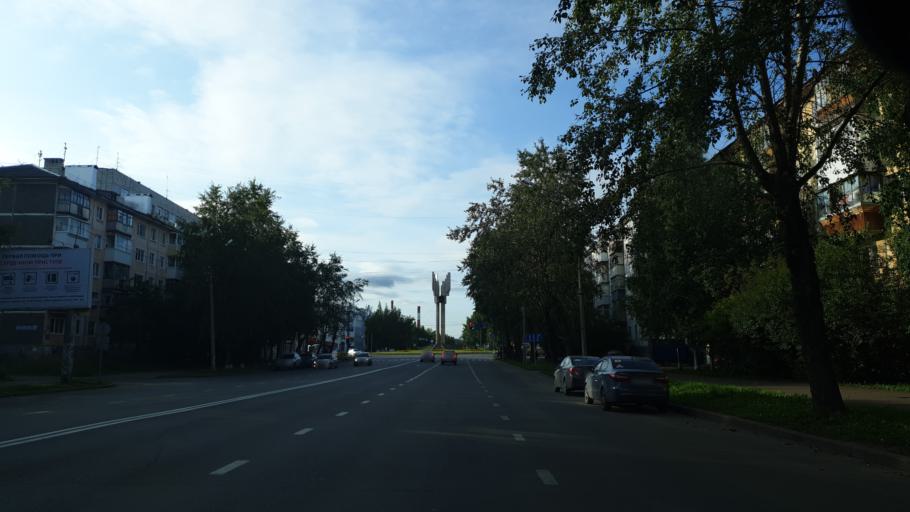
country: RU
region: Komi Republic
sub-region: Syktyvdinskiy Rayon
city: Syktyvkar
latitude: 61.6623
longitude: 50.8177
